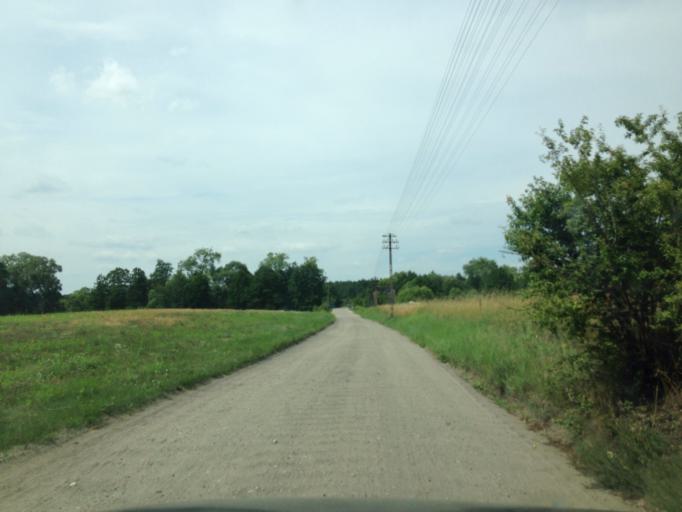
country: PL
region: Kujawsko-Pomorskie
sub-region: Powiat brodnicki
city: Brodnica
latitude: 53.2787
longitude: 19.4814
